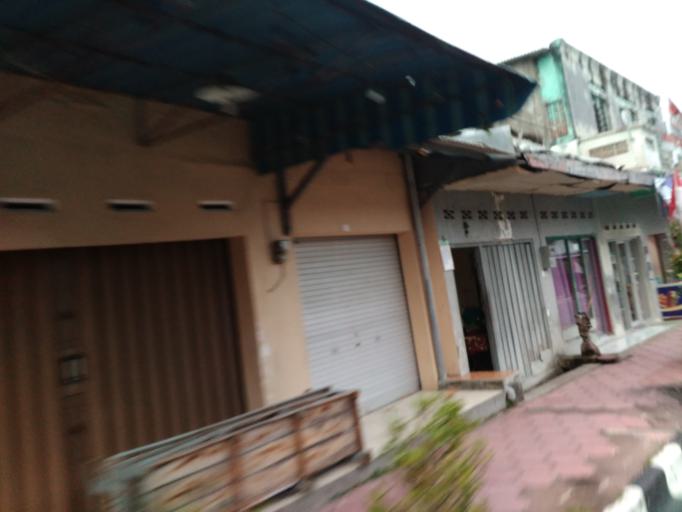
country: ID
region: Central Java
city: Boyolali
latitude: -7.5318
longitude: 110.6000
